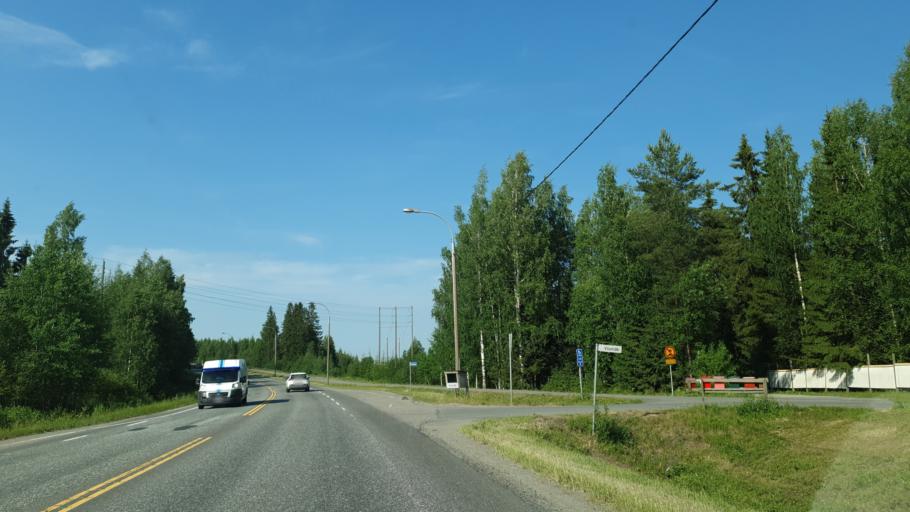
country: FI
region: Northern Savo
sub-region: Kuopio
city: Siilinjaervi
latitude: 63.1172
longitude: 27.7684
